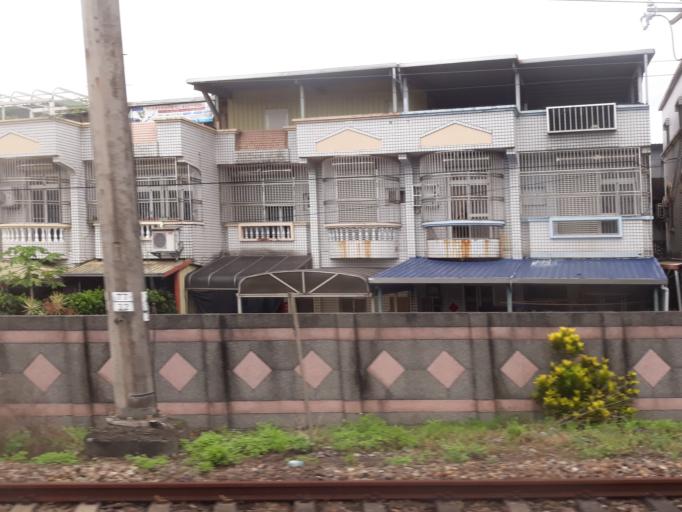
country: TW
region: Taiwan
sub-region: Yilan
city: Yilan
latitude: 24.7026
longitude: 121.7750
